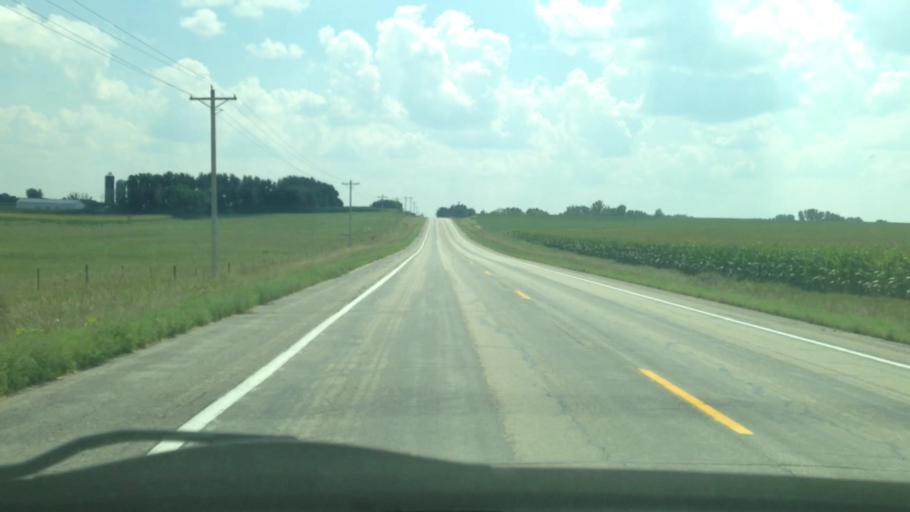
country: US
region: Minnesota
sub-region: Olmsted County
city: Rochester
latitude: 43.9340
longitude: -92.4087
